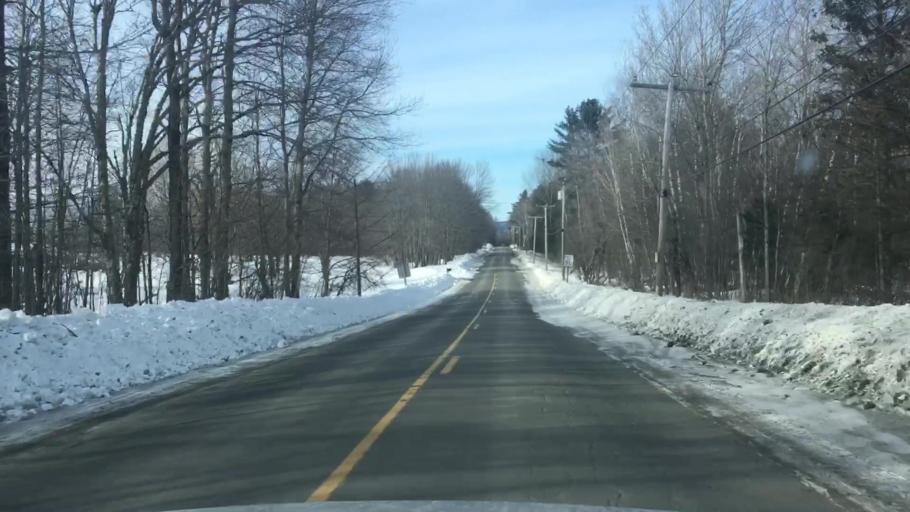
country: US
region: Maine
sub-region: Penobscot County
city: Charleston
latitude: 45.0323
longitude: -69.0317
